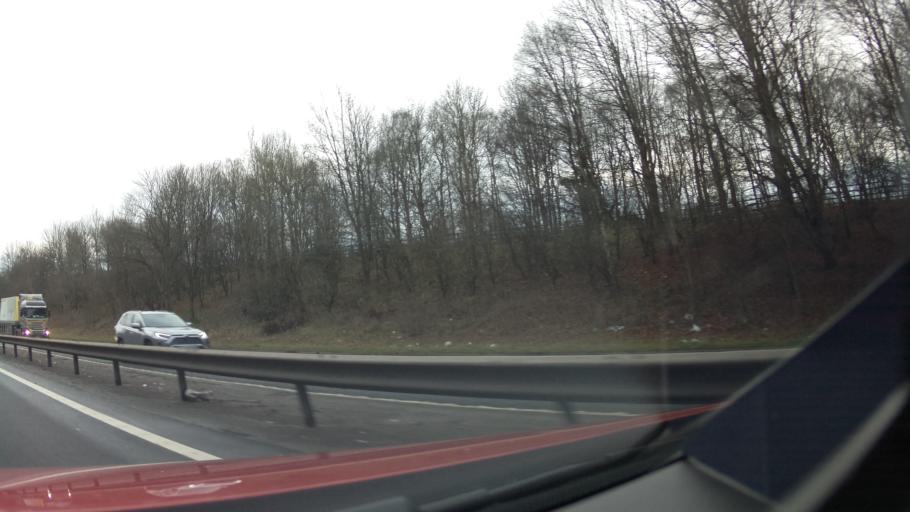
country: GB
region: Scotland
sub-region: North Lanarkshire
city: Motherwell
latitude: 55.7712
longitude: -4.0089
